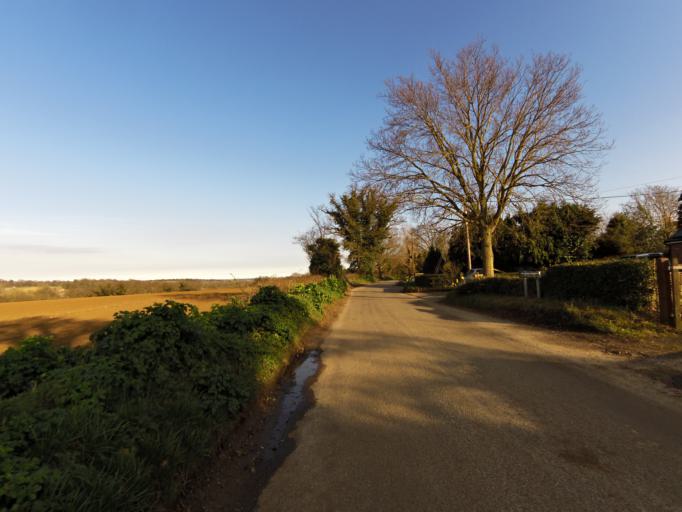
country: GB
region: England
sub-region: Suffolk
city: Kesgrave
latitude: 52.0887
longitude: 1.2484
